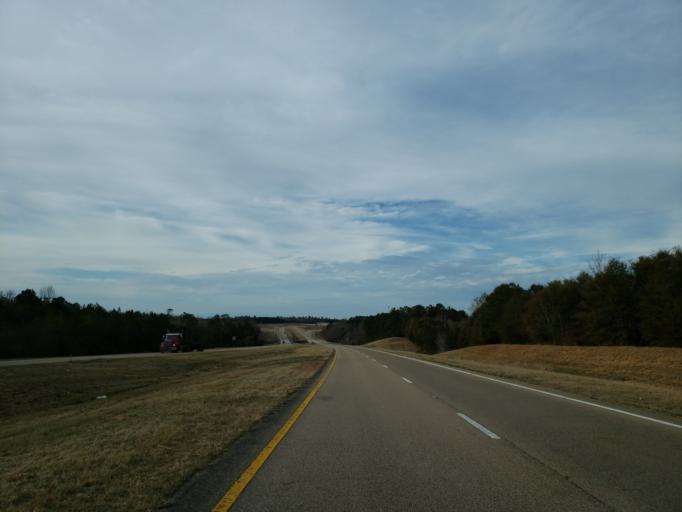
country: US
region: Mississippi
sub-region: Wayne County
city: Waynesboro
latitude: 31.6721
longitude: -88.6074
